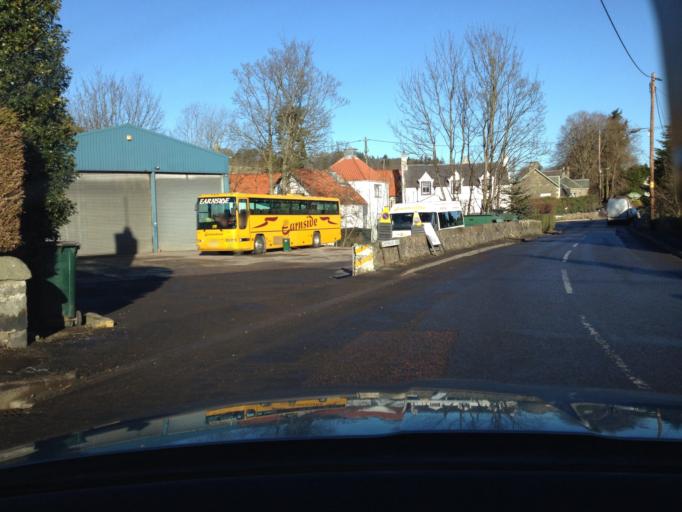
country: GB
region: Scotland
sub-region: Perth and Kinross
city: Milnathort
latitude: 56.2786
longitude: -3.4014
